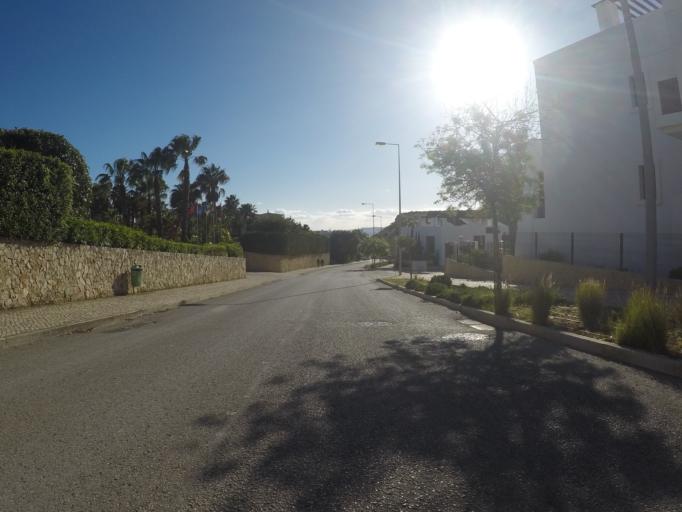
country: PT
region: Faro
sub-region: Lagos
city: Lagos
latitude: 37.0867
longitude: -8.6848
